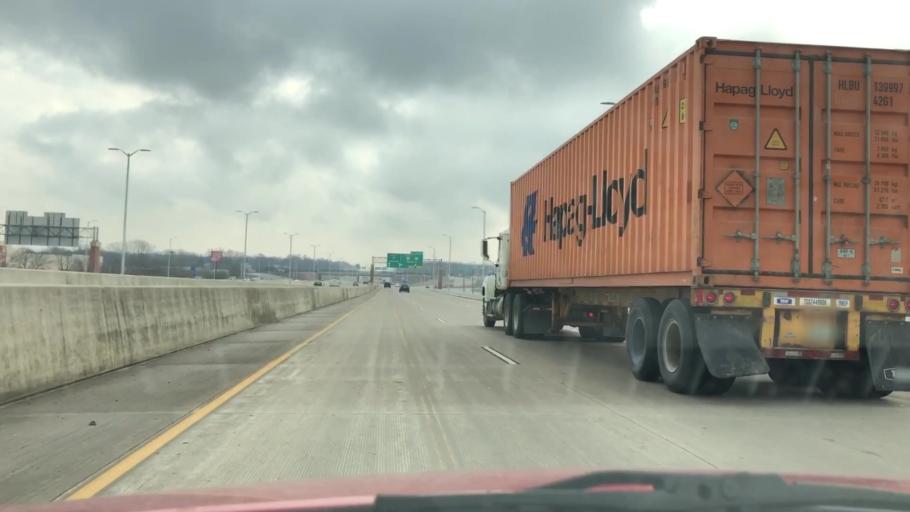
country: US
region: Wisconsin
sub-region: Brown County
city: Howard
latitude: 44.5297
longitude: -88.0819
